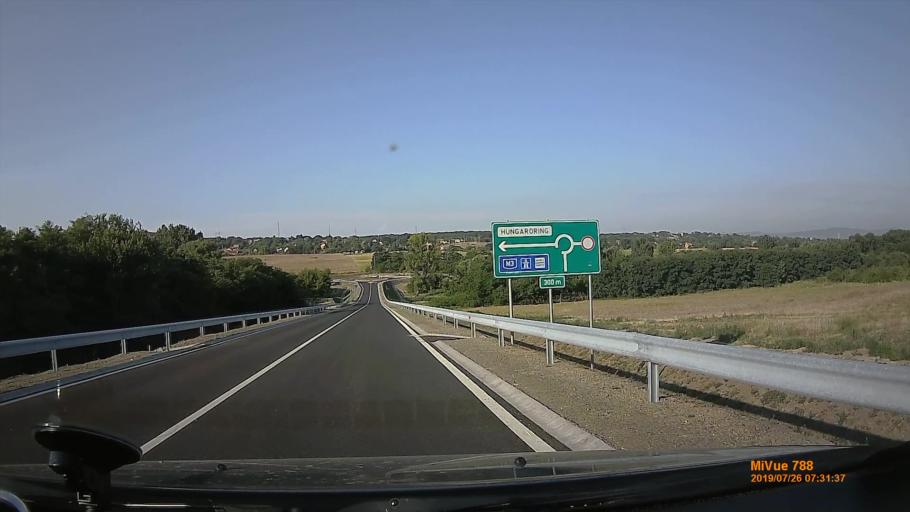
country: HU
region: Pest
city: Mogyorod
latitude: 47.5991
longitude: 19.2218
